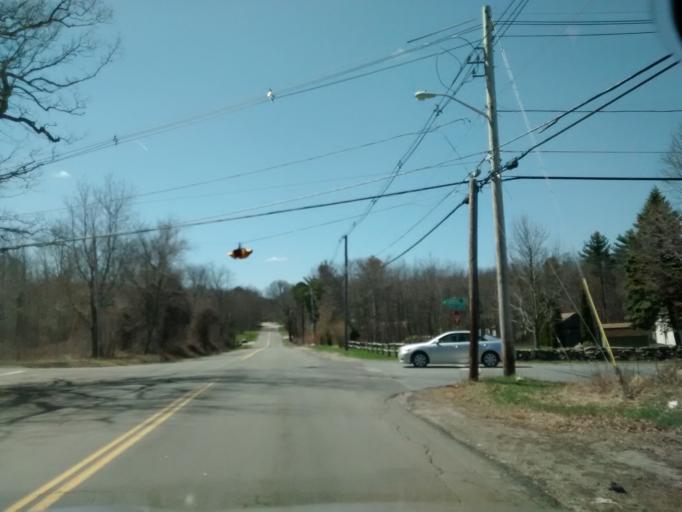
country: US
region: Massachusetts
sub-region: Worcester County
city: Sutton
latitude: 42.1383
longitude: -71.7461
